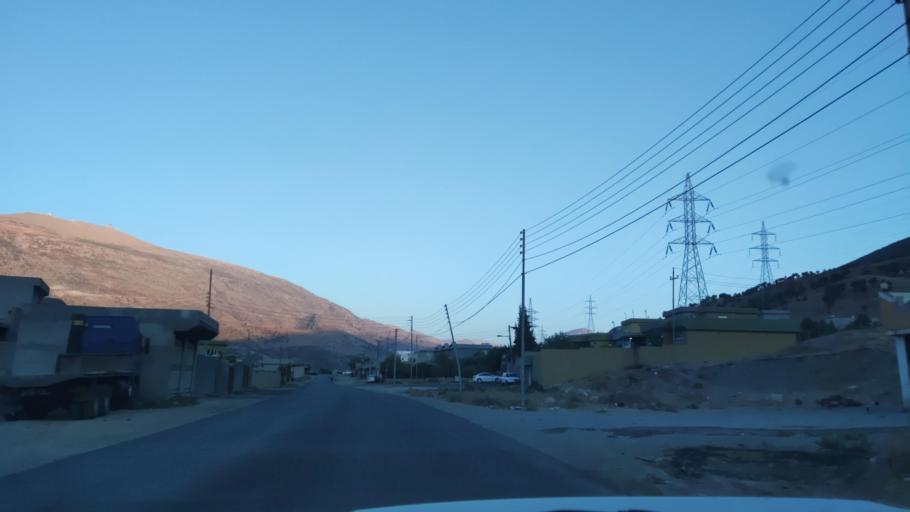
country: IQ
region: Arbil
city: Ruwandiz
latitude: 36.5912
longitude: 44.3864
